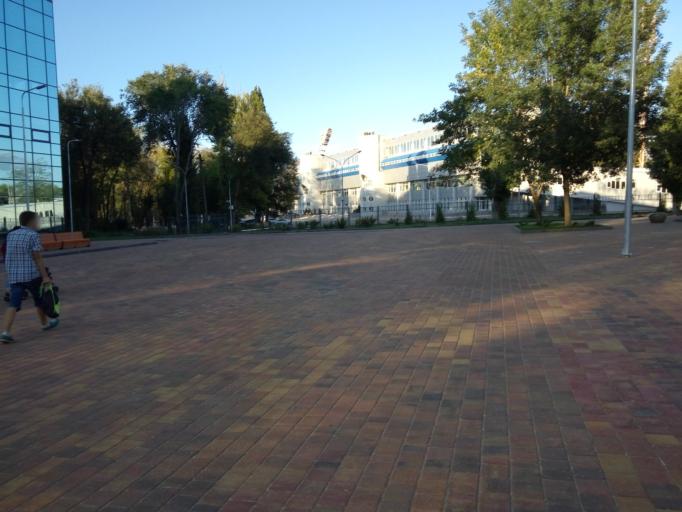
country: RU
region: Rostov
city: Rostov-na-Donu
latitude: 47.2419
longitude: 39.7585
